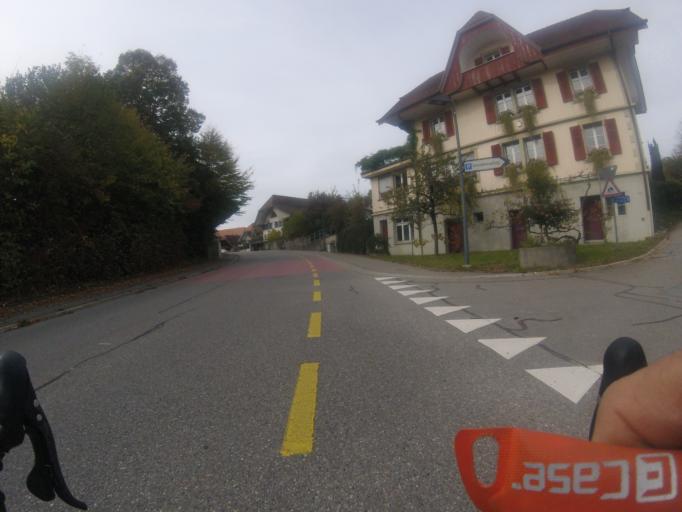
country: CH
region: Bern
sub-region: Bern-Mittelland District
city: Frauenkappelen
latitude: 46.9551
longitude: 7.3374
